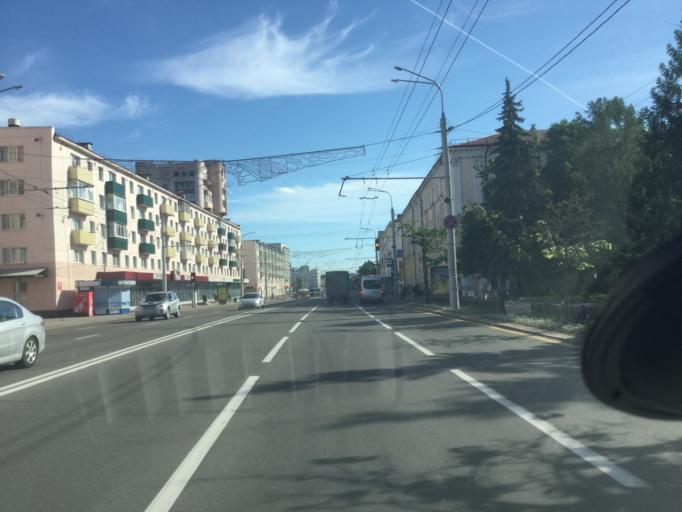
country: BY
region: Vitebsk
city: Vitebsk
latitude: 55.1871
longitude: 30.2050
